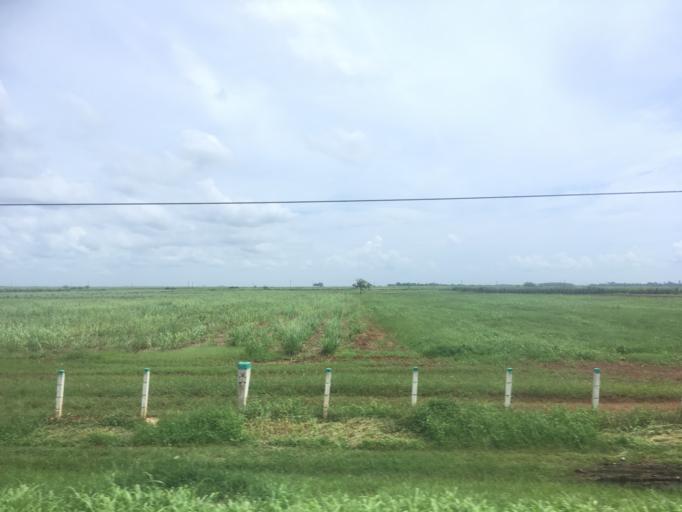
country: CU
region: Matanzas
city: Jovellanos
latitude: 22.7974
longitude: -81.1513
